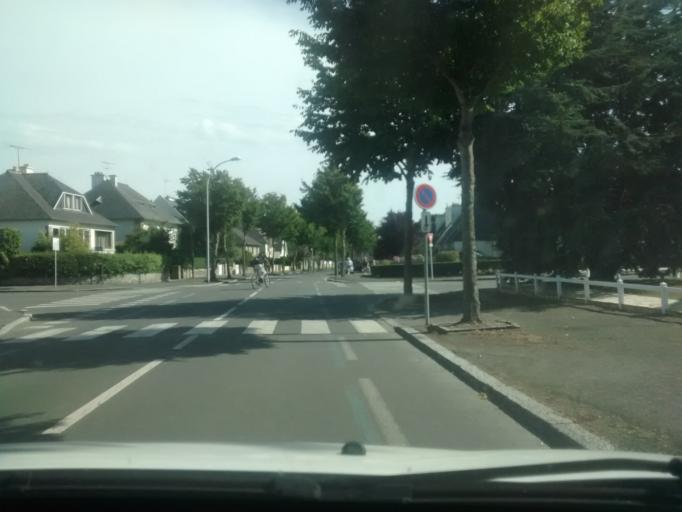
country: FR
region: Brittany
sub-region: Departement d'Ille-et-Vilaine
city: Saint-Malo
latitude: 48.6682
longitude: -1.9799
